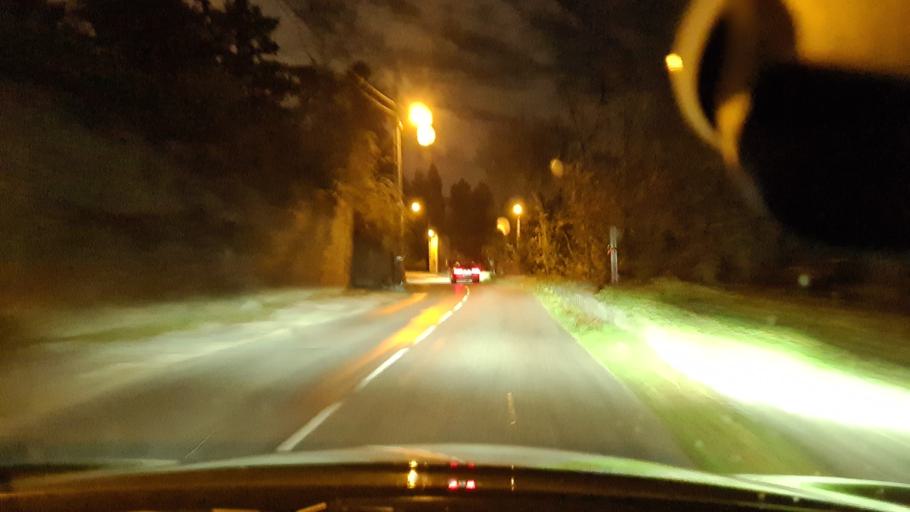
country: FR
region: Rhone-Alpes
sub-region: Departement du Rhone
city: Limonest
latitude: 45.8243
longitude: 4.7888
